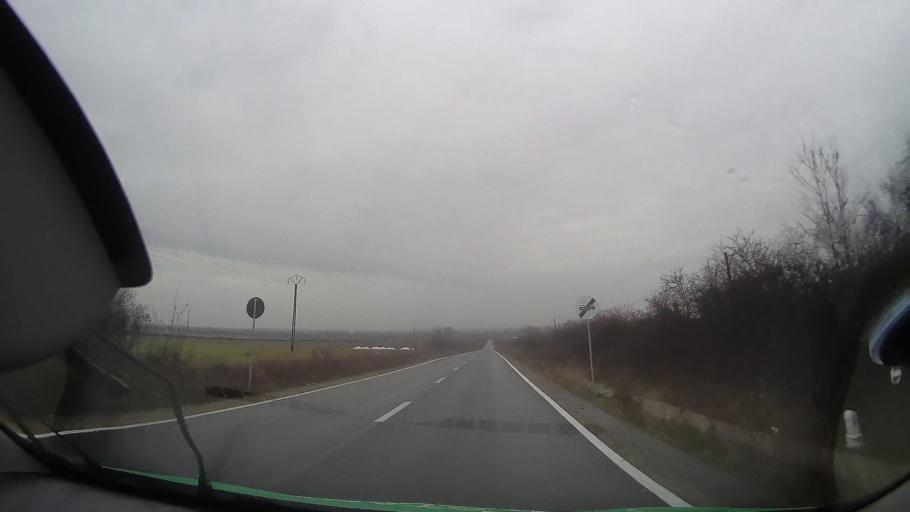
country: RO
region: Bihor
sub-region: Comuna Olcea
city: Olcea
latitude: 46.7173
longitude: 21.9535
